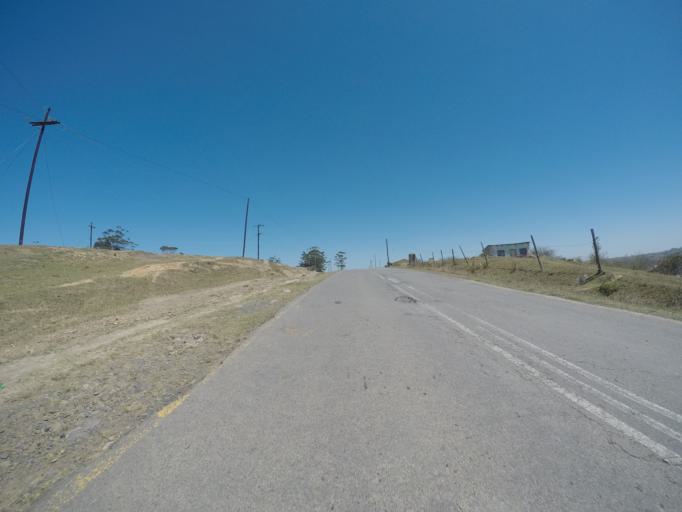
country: ZA
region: Eastern Cape
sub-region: OR Tambo District Municipality
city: Libode
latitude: -31.9164
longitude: 28.9812
